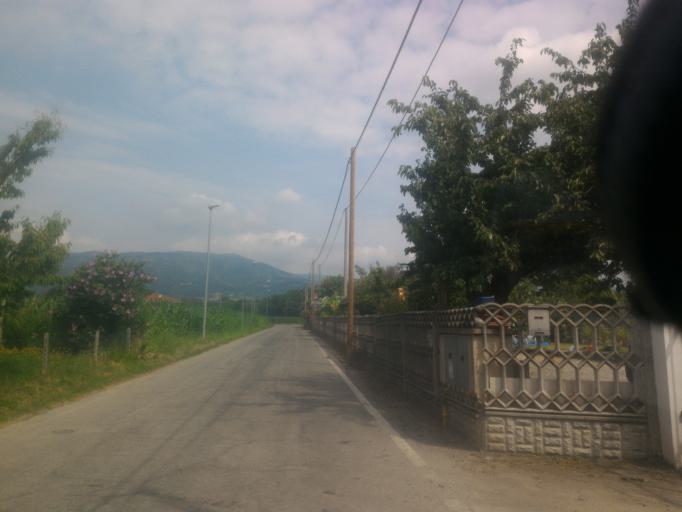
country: IT
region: Piedmont
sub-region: Provincia di Torino
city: Pinerolo
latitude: 44.8693
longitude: 7.3190
